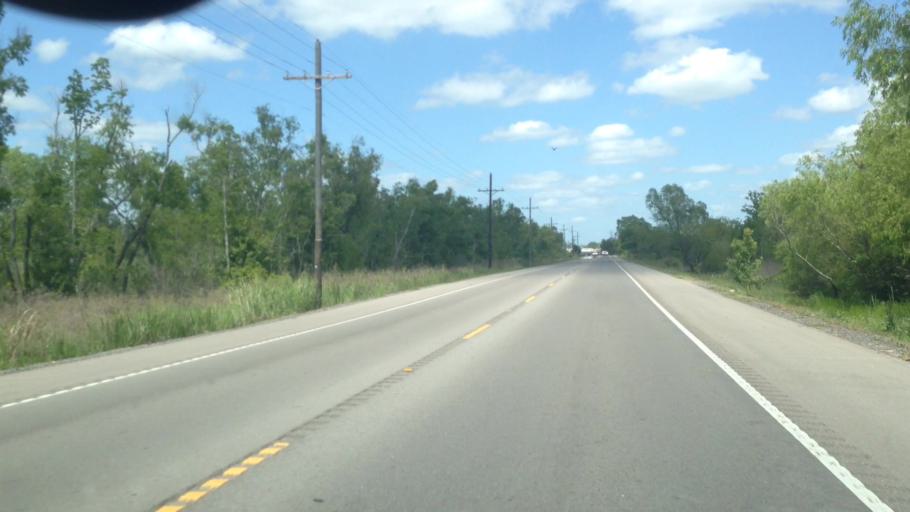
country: US
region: Louisiana
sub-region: Terrebonne Parish
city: Houma
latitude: 29.6372
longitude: -90.6972
